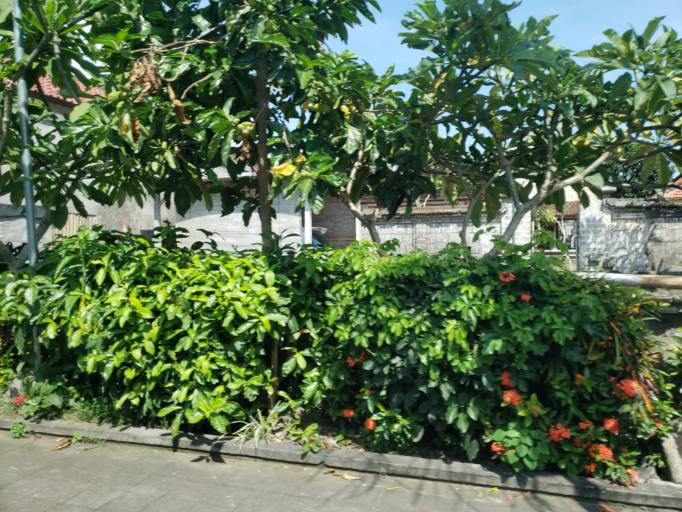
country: ID
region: Bali
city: Kangin
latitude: -8.8325
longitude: 115.1264
